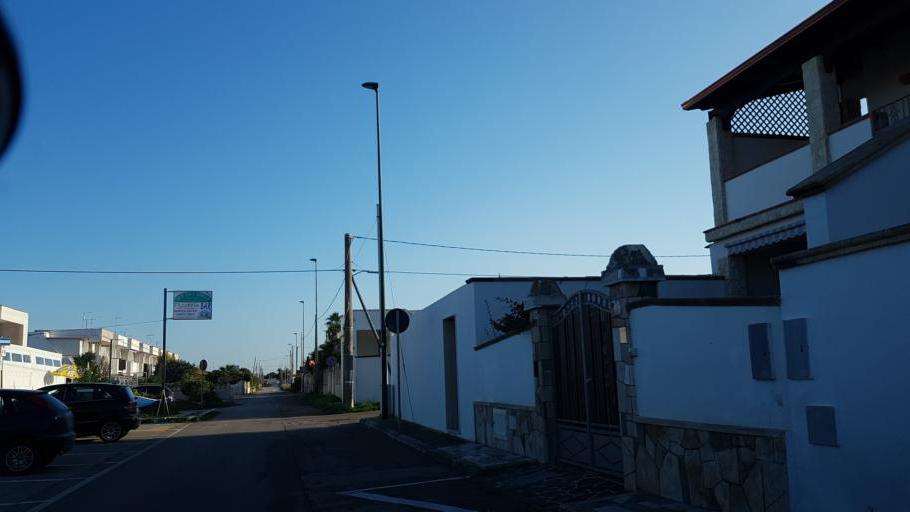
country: IT
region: Apulia
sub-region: Provincia di Brindisi
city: Torchiarolo
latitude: 40.5165
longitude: 18.0930
